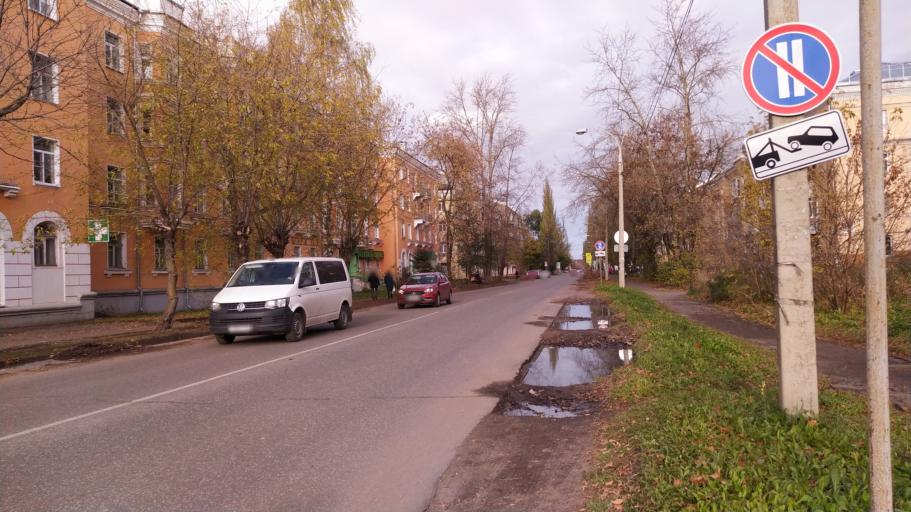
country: RU
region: Jaroslavl
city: Rybinsk
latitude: 58.0567
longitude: 38.8107
